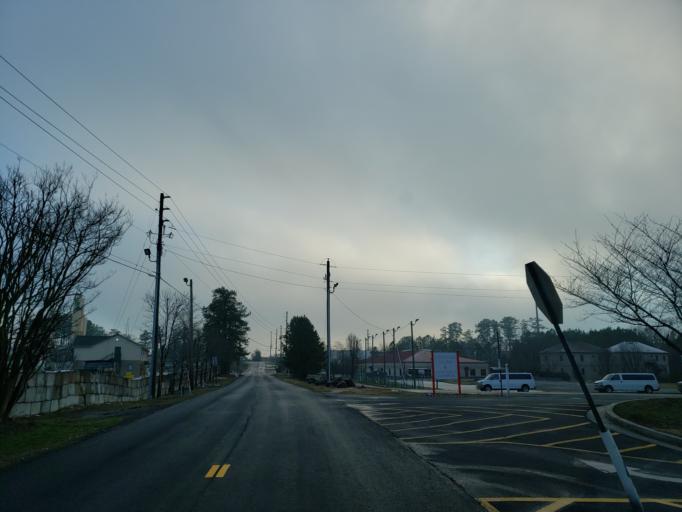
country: US
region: Georgia
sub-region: Cobb County
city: Kennesaw
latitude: 34.0241
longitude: -84.5927
